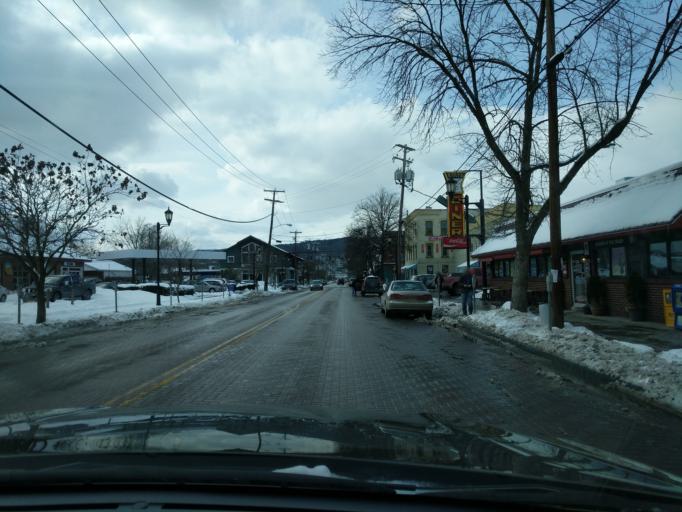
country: US
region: New York
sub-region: Tompkins County
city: Ithaca
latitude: 42.4394
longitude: -76.5048
